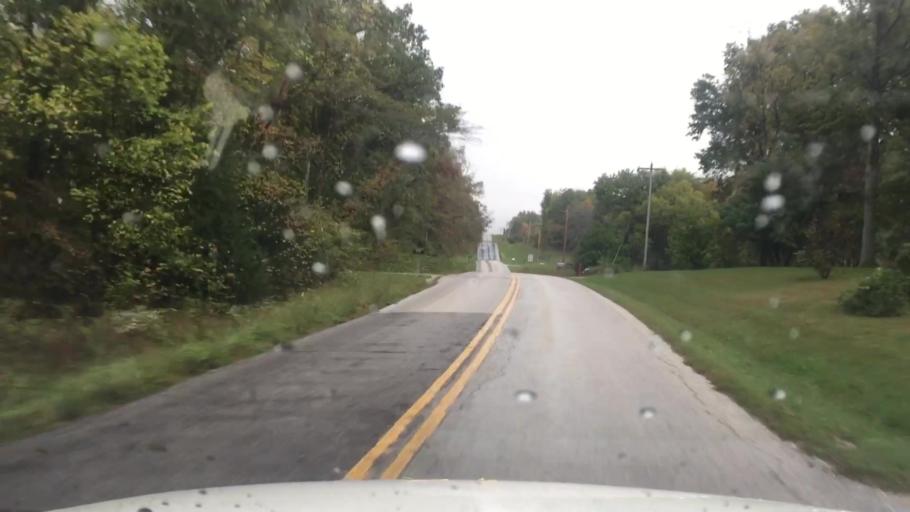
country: US
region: Missouri
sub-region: Boone County
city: Columbia
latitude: 38.9458
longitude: -92.4962
